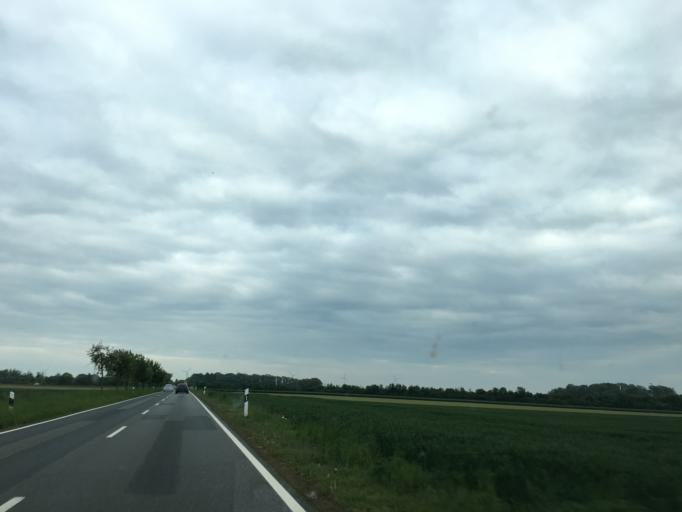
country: DE
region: Lower Saxony
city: Gross Munzel
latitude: 52.3877
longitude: 9.4643
